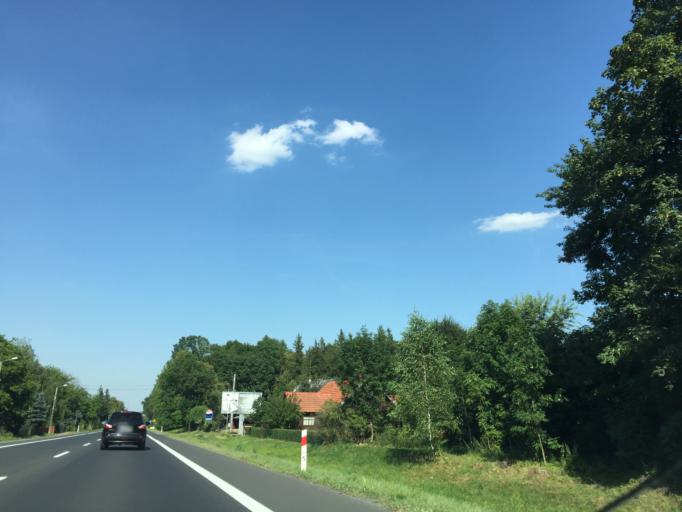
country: PL
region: Lesser Poland Voivodeship
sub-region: Powiat krakowski
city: Slomniki
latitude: 50.2175
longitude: 20.0303
